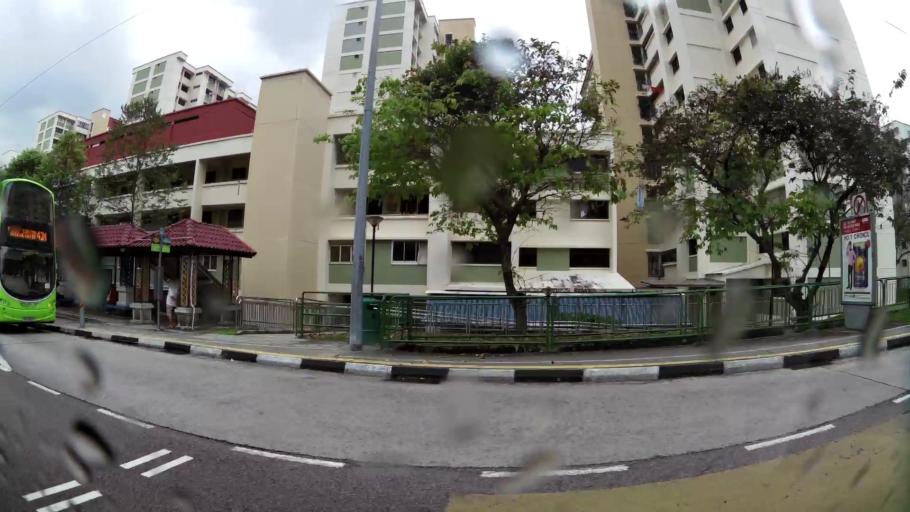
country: SG
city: Singapore
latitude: 1.3576
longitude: 103.8738
